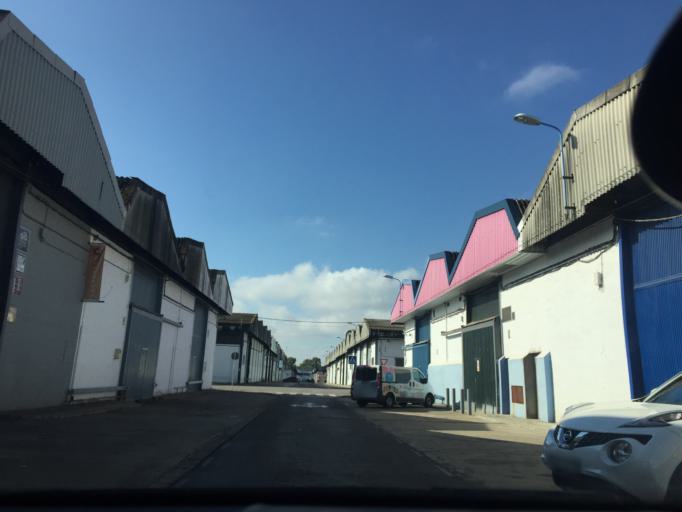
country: ES
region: Andalusia
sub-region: Provincia de Sevilla
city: Sevilla
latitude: 37.3678
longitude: -5.9577
